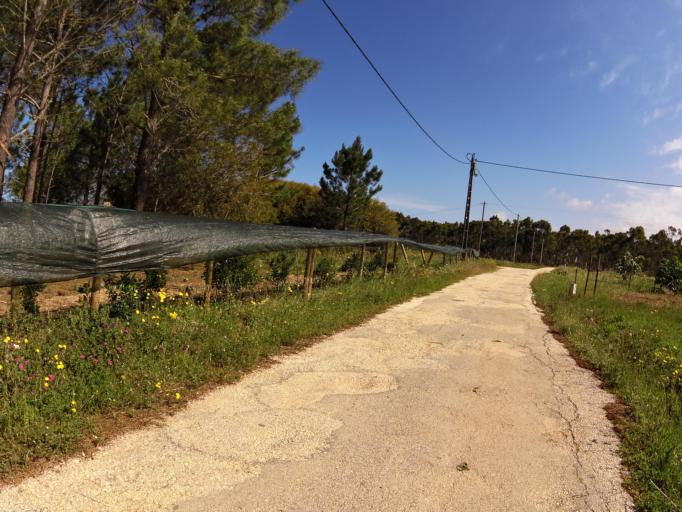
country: PT
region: Faro
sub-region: Aljezur
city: Aljezur
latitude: 37.3371
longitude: -8.8084
